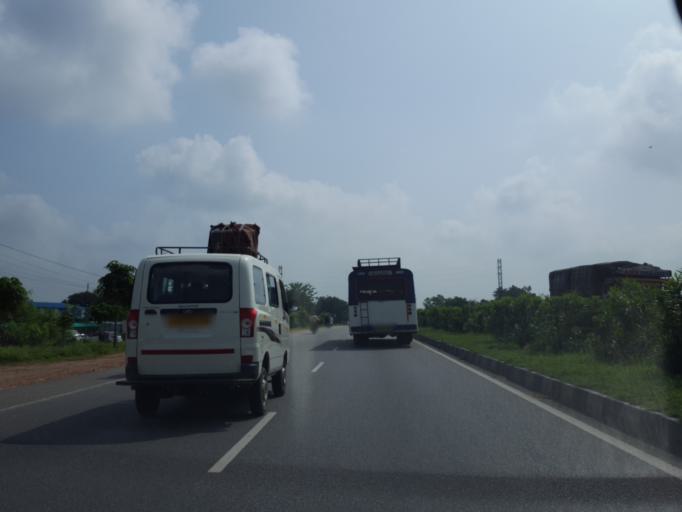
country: IN
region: Telangana
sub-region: Nalgonda
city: Gudur
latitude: 17.2585
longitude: 78.8509
